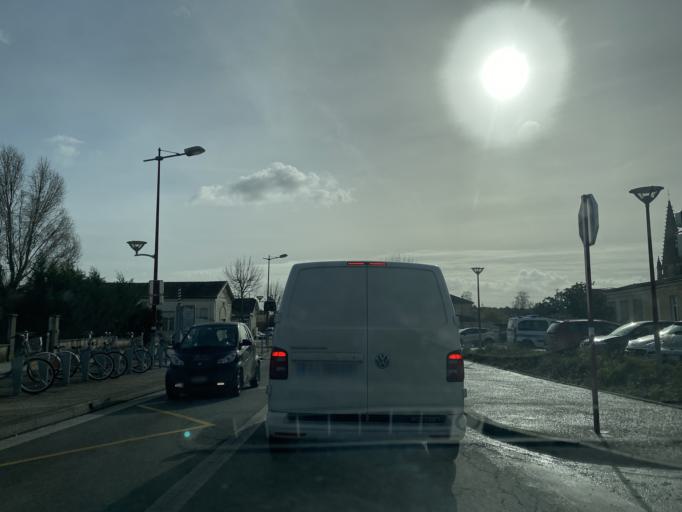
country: FR
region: Aquitaine
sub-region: Departement de la Gironde
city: Le Taillan-Medoc
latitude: 44.9049
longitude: -0.6690
